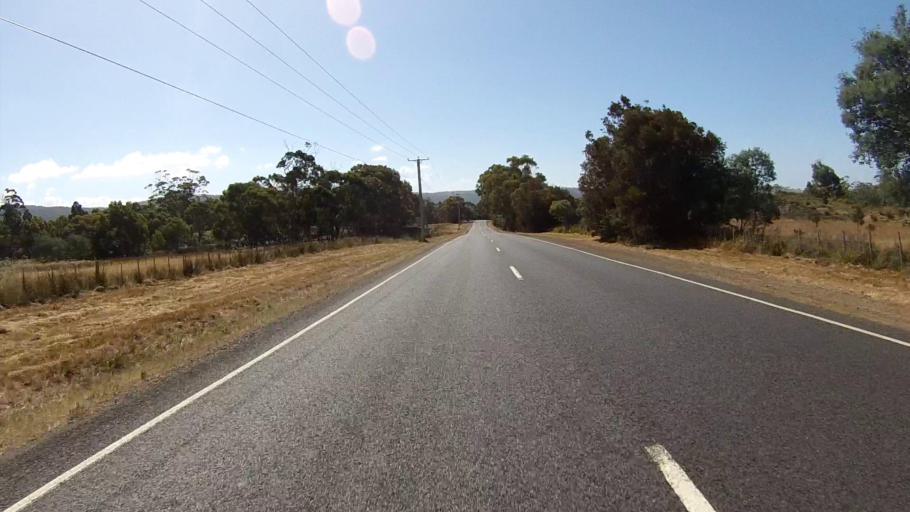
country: AU
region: Tasmania
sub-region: Sorell
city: Sorell
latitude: -42.5325
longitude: 147.8972
